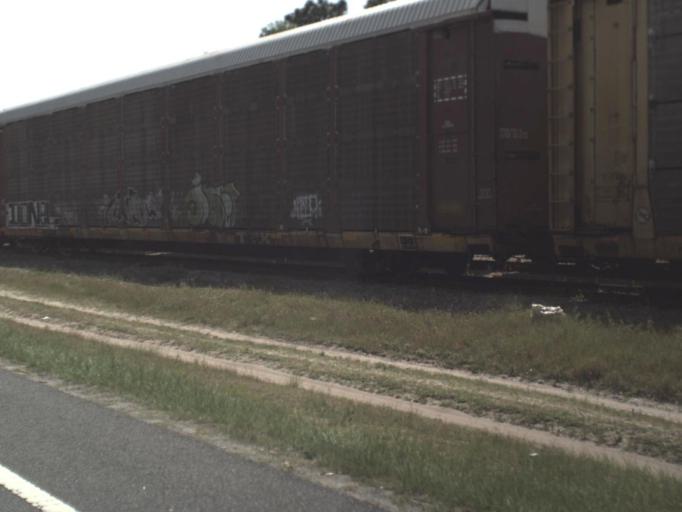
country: US
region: Florida
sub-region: Duval County
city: Jacksonville
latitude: 30.4537
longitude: -81.6372
